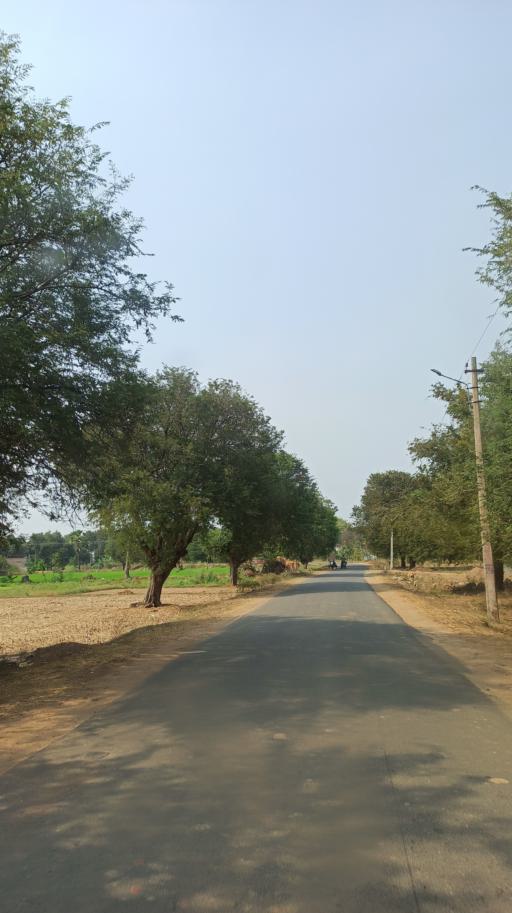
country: IN
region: Tamil Nadu
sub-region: Tiruvannamalai
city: Desur
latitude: 12.4589
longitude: 79.3730
